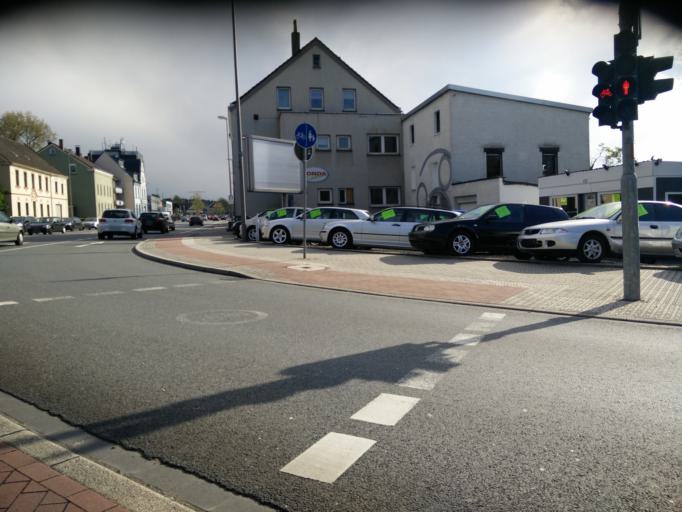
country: DE
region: North Rhine-Westphalia
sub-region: Regierungsbezirk Arnsberg
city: Herne
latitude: 51.5161
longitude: 7.2120
